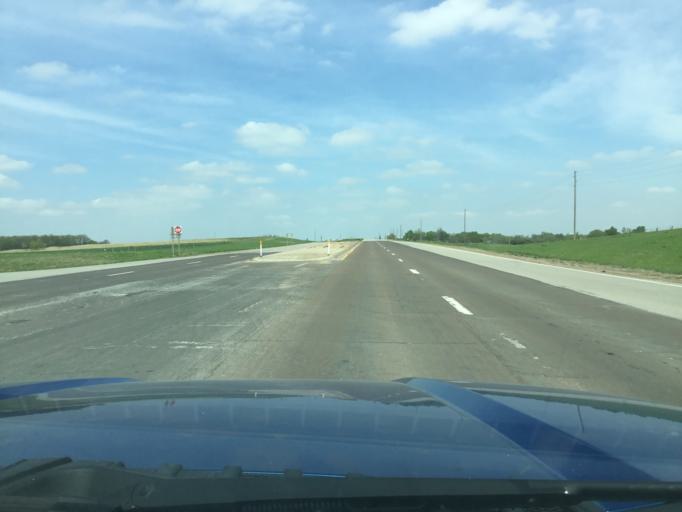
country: US
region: Kansas
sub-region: Osage County
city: Carbondale
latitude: 38.9077
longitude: -95.6873
